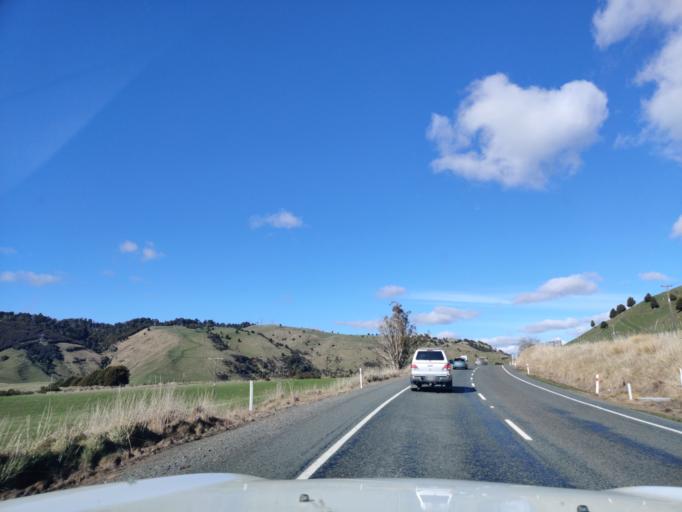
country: NZ
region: Manawatu-Wanganui
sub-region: Ruapehu District
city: Waiouru
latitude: -39.5542
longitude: 175.6954
